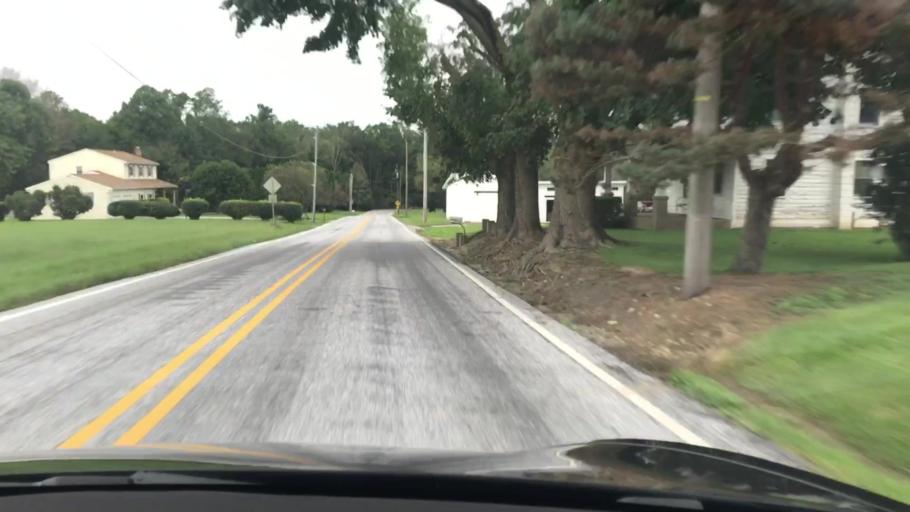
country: US
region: Pennsylvania
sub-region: York County
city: Dillsburg
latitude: 40.0611
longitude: -77.0828
